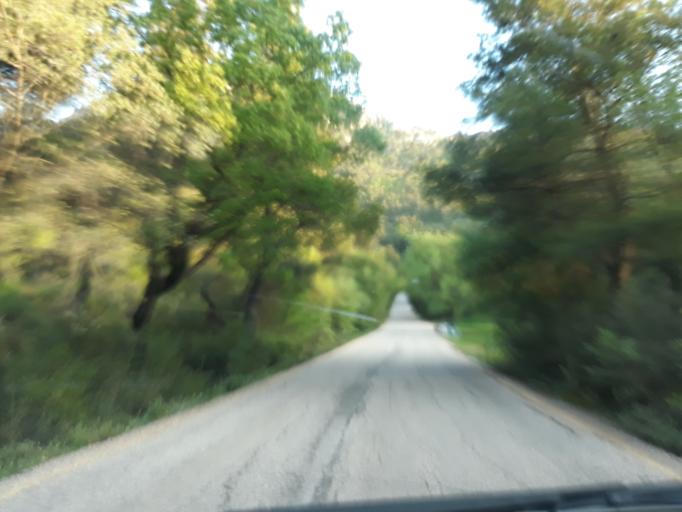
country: GR
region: Attica
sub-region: Nomarchia Anatolikis Attikis
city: Afidnes
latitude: 38.1927
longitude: 23.7836
